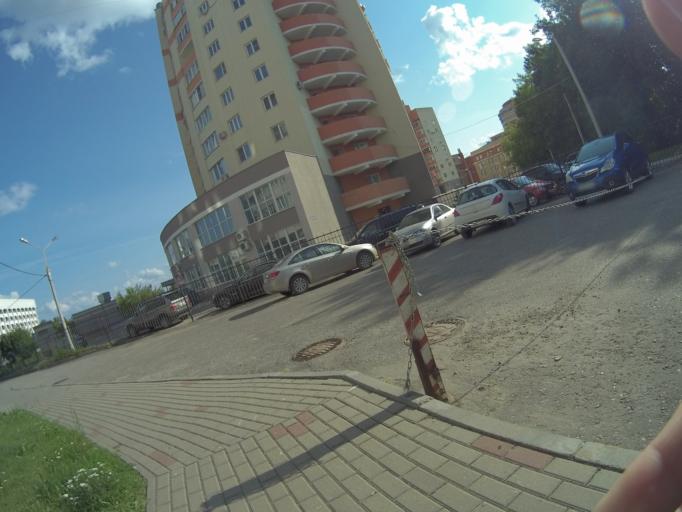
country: RU
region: Vladimir
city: Vladimir
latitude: 56.1389
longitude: 40.3866
